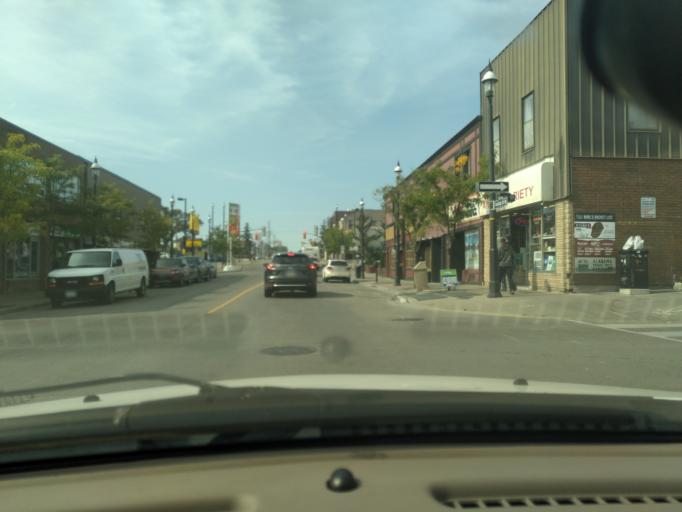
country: CA
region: Ontario
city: Barrie
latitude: 44.3884
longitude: -79.6923
